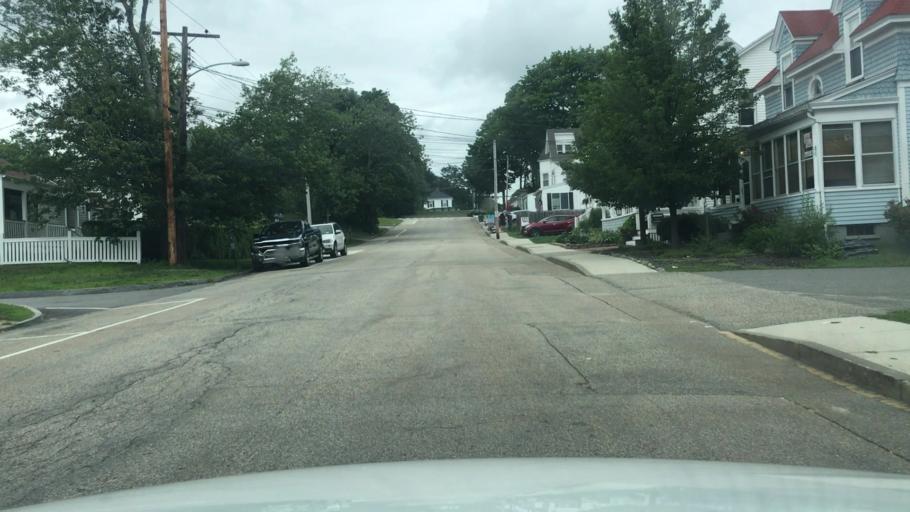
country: US
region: Maine
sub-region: York County
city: Old Orchard Beach
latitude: 43.5159
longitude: -70.3764
